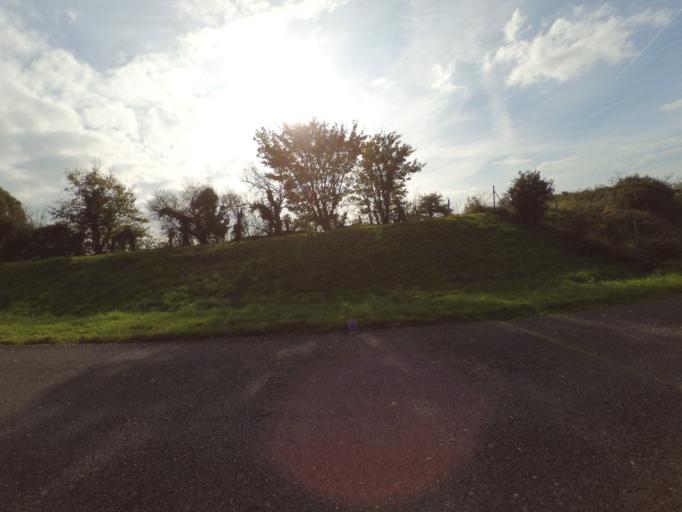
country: FR
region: Pays de la Loire
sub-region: Departement de la Loire-Atlantique
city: La Planche
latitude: 46.9977
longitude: -1.3829
